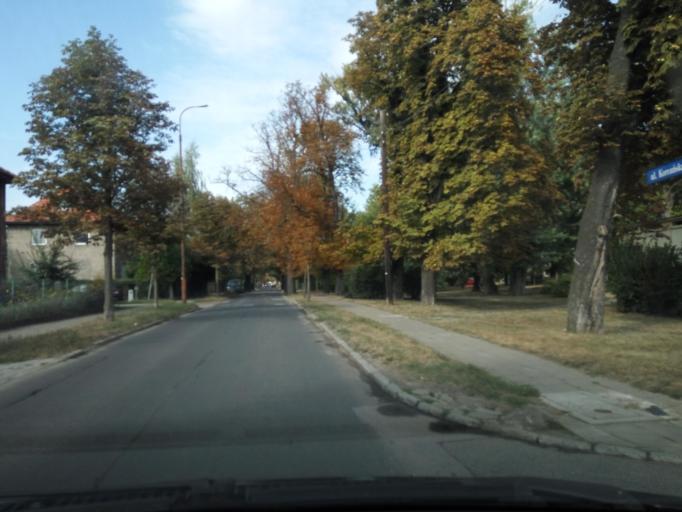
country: PL
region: Lower Silesian Voivodeship
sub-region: Powiat wroclawski
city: Radwanice
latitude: 51.0550
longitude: 17.0853
